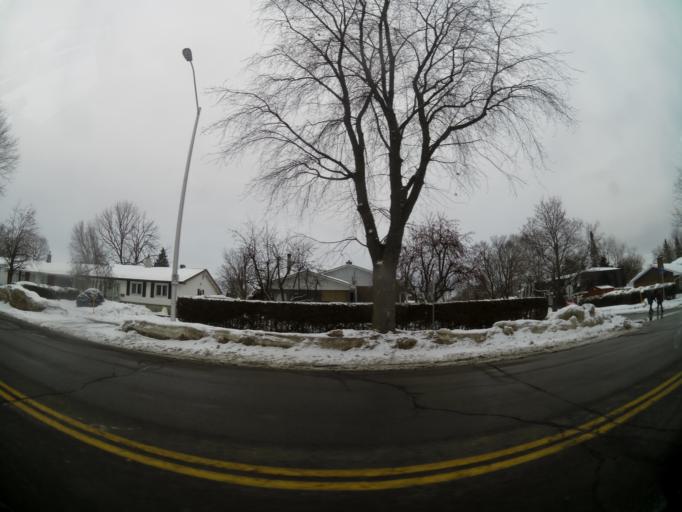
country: CA
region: Quebec
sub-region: Outaouais
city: Gatineau
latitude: 45.4563
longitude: -75.5993
